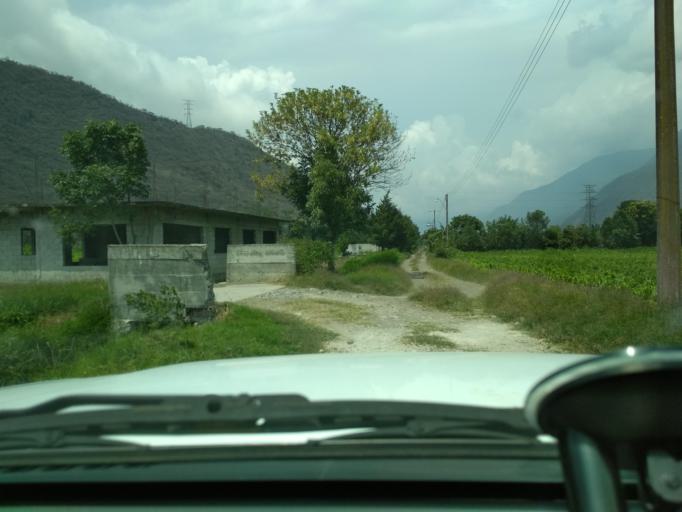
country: MX
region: Veracruz
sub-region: Nogales
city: Taza de Agua Ojo Zarco
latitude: 18.7792
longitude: -97.2173
